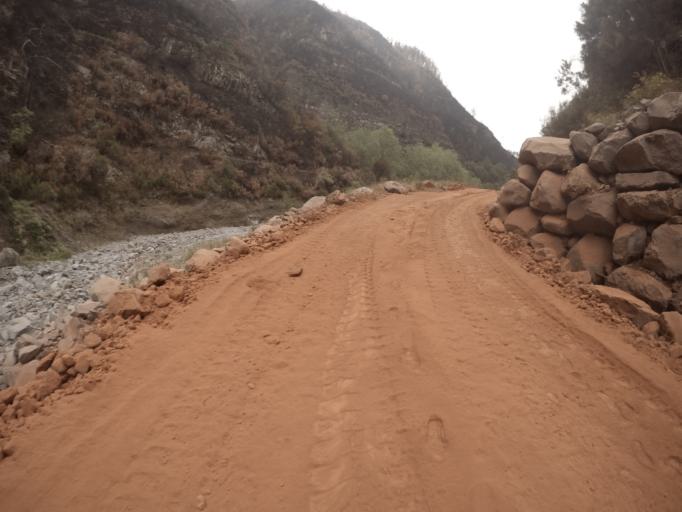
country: PT
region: Madeira
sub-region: Funchal
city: Nossa Senhora do Monte
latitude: 32.6953
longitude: -16.9174
